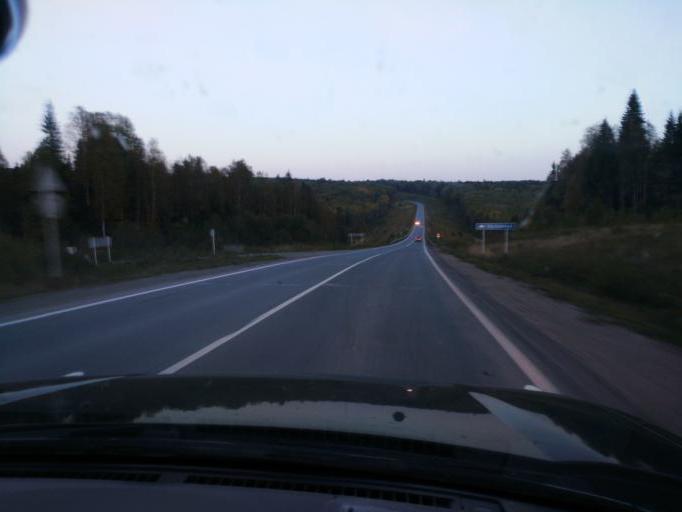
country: RU
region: Perm
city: Sylva
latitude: 58.3017
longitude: 56.7890
